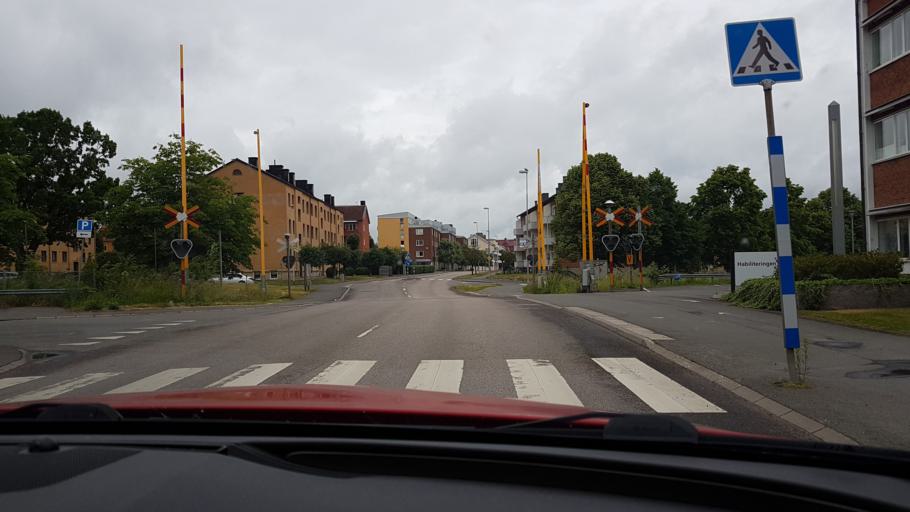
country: SE
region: Vaestra Goetaland
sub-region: Skovde Kommun
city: Skoevde
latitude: 58.3805
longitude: 13.8425
